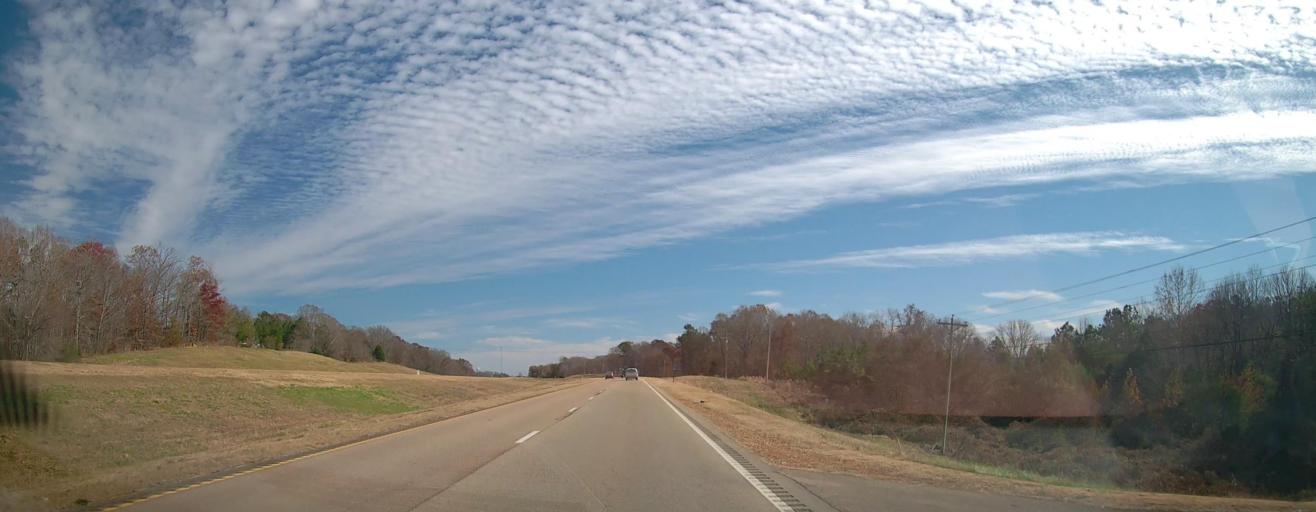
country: US
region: Mississippi
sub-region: Tippah County
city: Ripley
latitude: 34.9508
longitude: -88.8277
